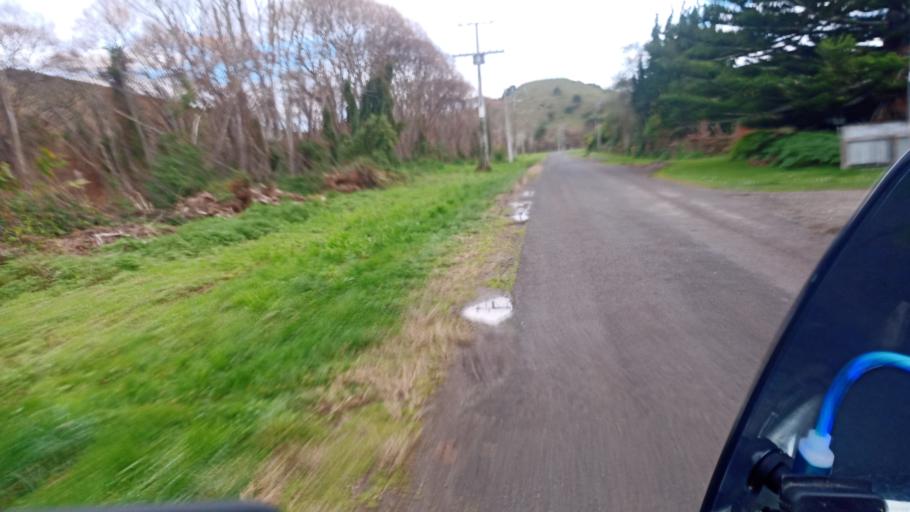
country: NZ
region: Gisborne
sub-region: Gisborne District
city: Gisborne
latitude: -38.3720
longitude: 178.2891
